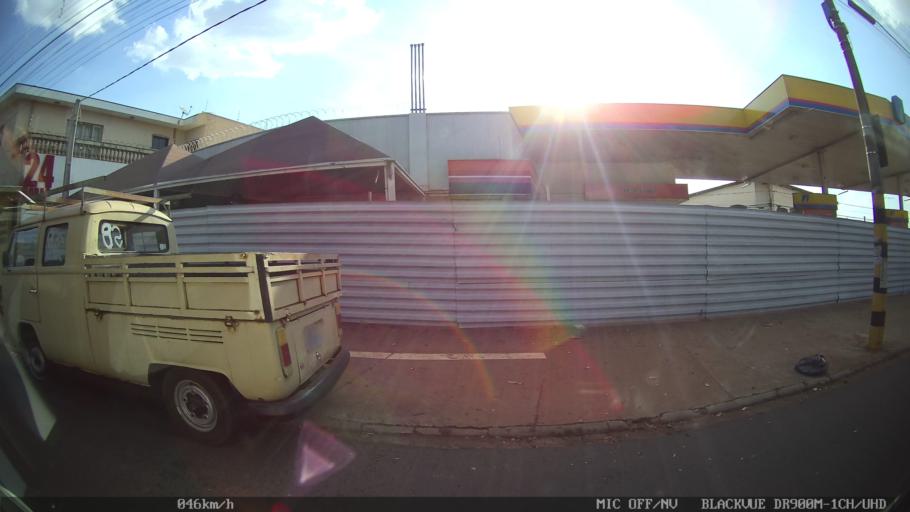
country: BR
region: Sao Paulo
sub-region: Ribeirao Preto
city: Ribeirao Preto
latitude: -21.1504
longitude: -47.8041
